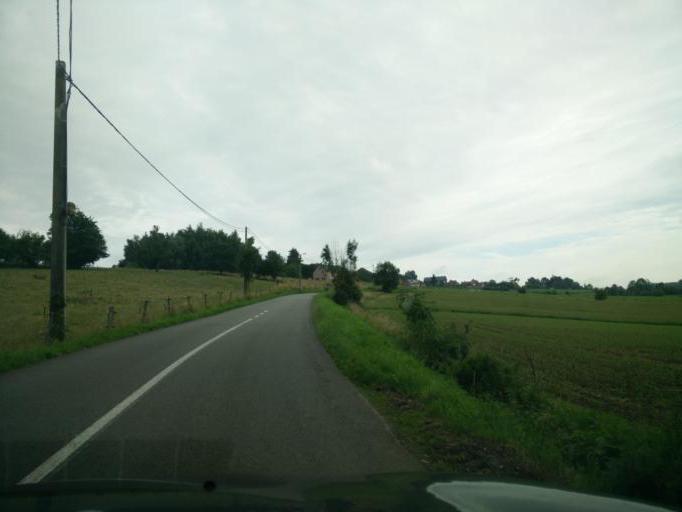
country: BE
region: Wallonia
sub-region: Province du Hainaut
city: Flobecq
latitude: 50.7521
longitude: 3.7294
